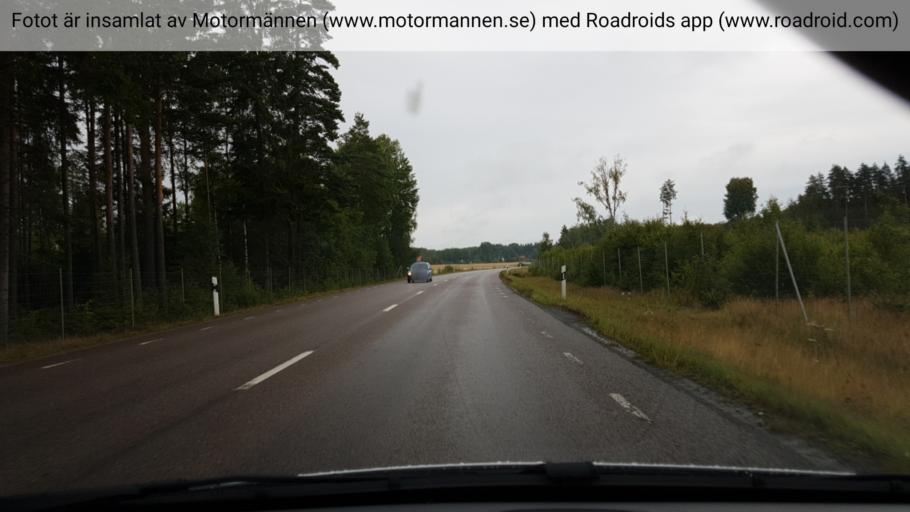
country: SE
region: Vaestra Goetaland
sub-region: Tibro Kommun
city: Tibro
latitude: 58.4393
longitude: 14.1777
